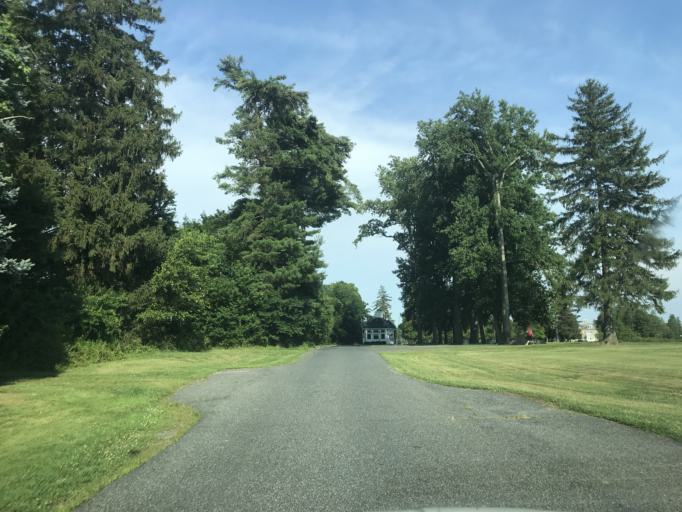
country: US
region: Maryland
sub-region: Harford County
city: Aberdeen Proving Ground
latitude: 39.5049
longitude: -76.1179
